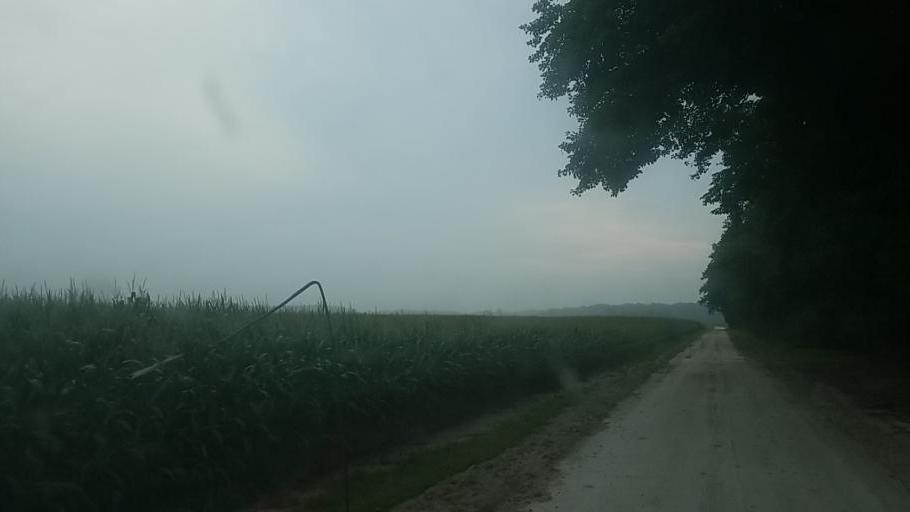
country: US
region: Maryland
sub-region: Wicomico County
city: Pittsville
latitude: 38.4447
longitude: -75.4335
